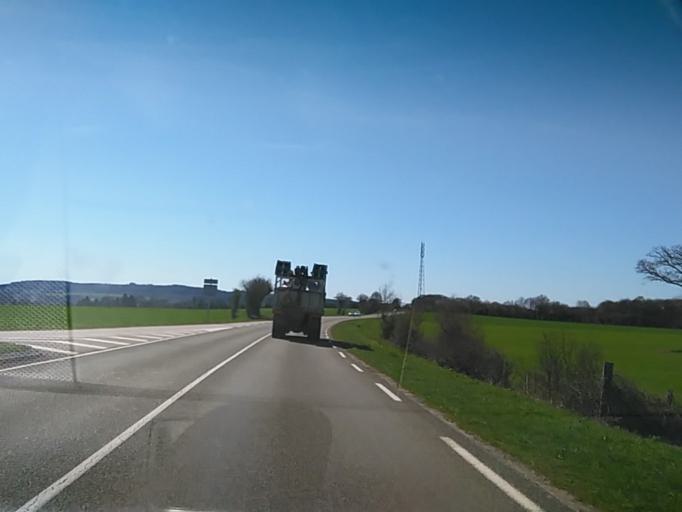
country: FR
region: Pays de la Loire
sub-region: Departement de la Mayenne
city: Pre-en-Pail
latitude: 48.5650
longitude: -0.1200
